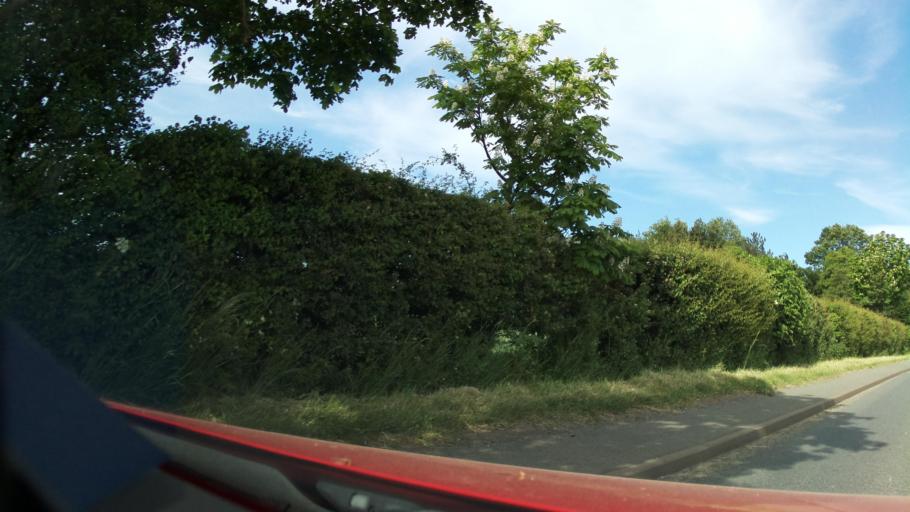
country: GB
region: England
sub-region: Worcestershire
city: Badsey
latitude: 52.0939
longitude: -1.8790
